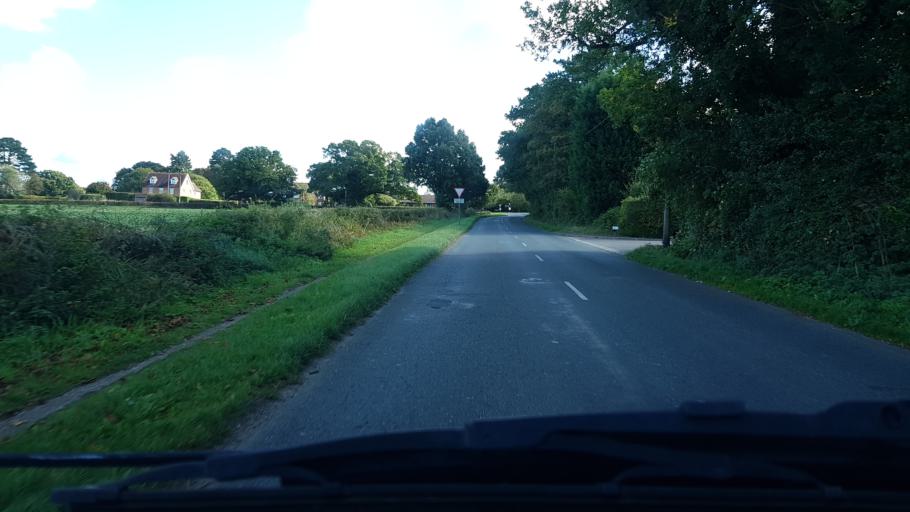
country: GB
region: England
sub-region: West Sussex
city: Rudgwick
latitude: 51.0637
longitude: -0.5186
